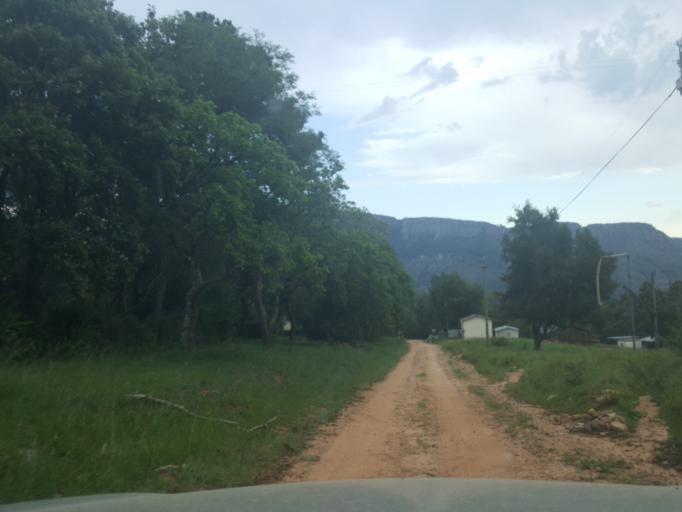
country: ZA
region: Limpopo
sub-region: Mopani District Municipality
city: Hoedspruit
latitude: -24.5839
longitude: 30.8626
